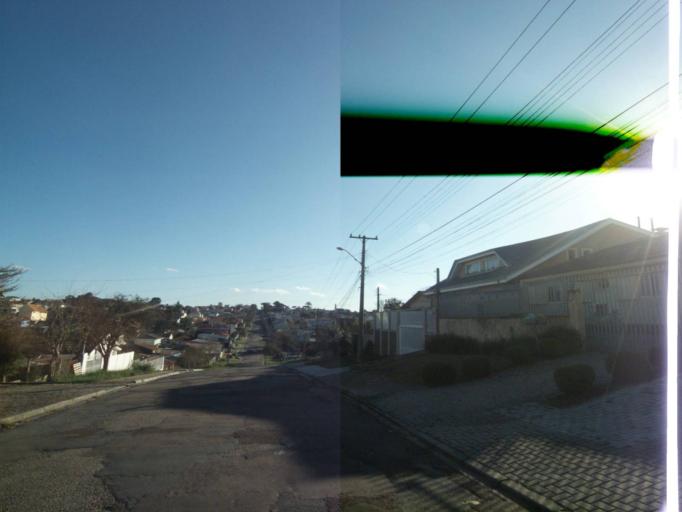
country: BR
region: Parana
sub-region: Curitiba
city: Curitiba
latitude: -25.3841
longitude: -49.2505
